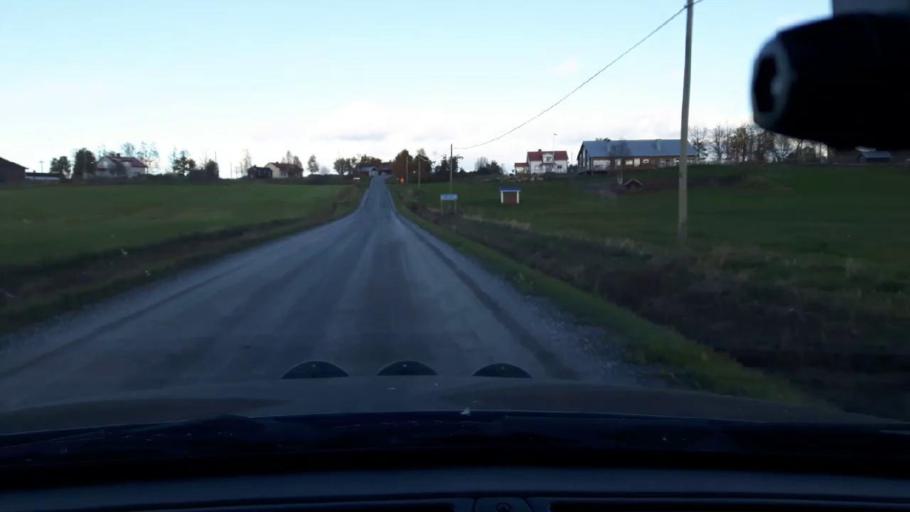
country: SE
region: Jaemtland
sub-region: Krokoms Kommun
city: Krokom
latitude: 63.0776
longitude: 14.2730
